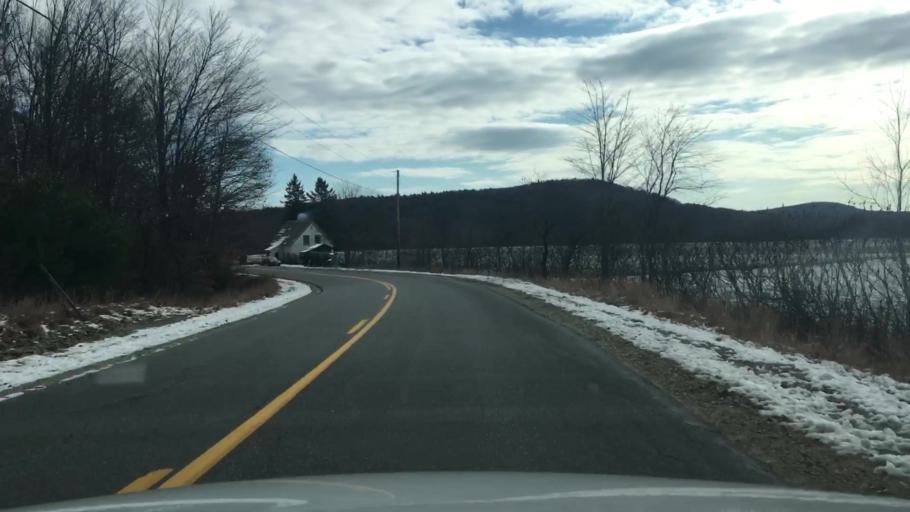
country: US
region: Maine
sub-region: Oxford County
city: Canton
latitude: 44.4692
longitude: -70.3068
